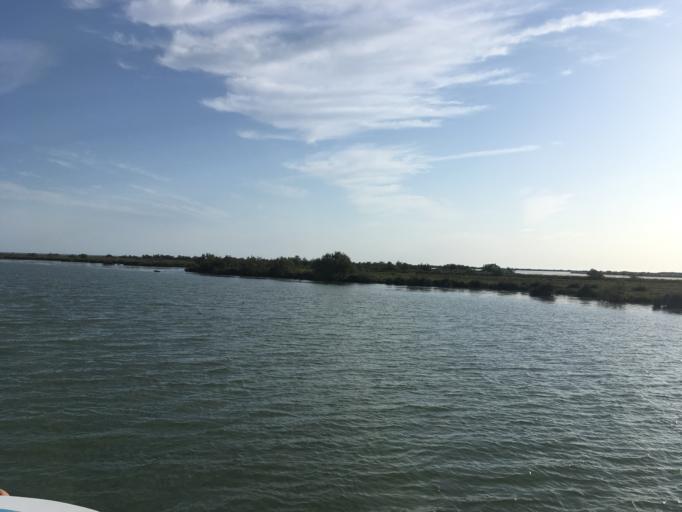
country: FR
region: Provence-Alpes-Cote d'Azur
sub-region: Departement des Bouches-du-Rhone
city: Saintes-Maries-de-la-Mer
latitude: 43.4606
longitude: 4.3897
